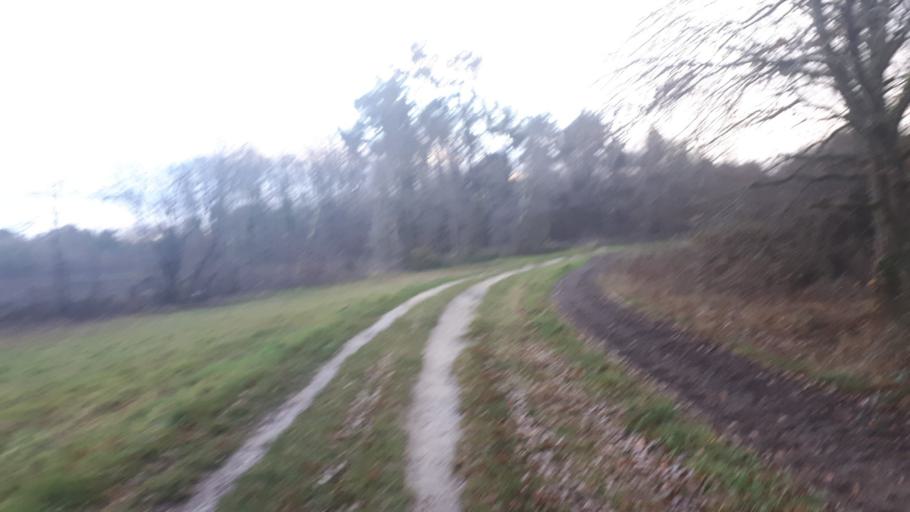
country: FR
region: Centre
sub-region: Departement du Loir-et-Cher
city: Saint-Romain-sur-Cher
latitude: 47.3454
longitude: 1.3952
